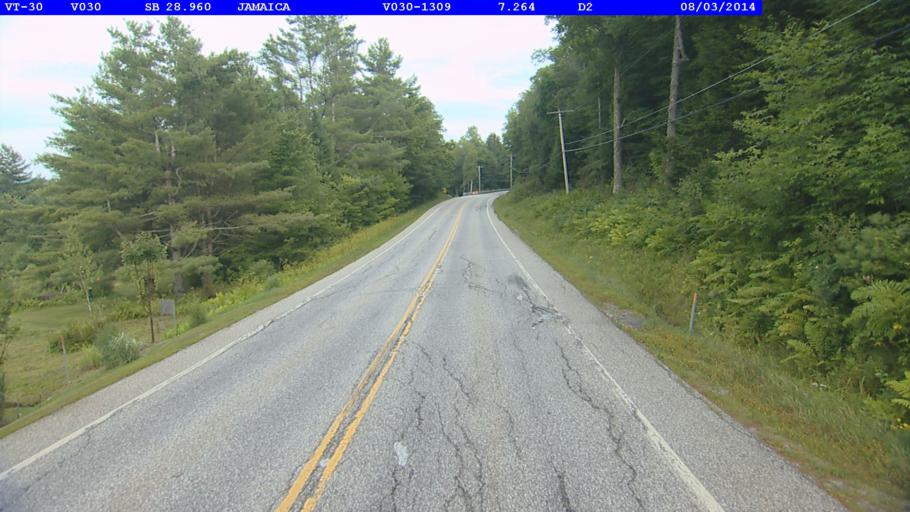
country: US
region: Vermont
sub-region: Windham County
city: Dover
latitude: 43.1337
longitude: -72.8180
